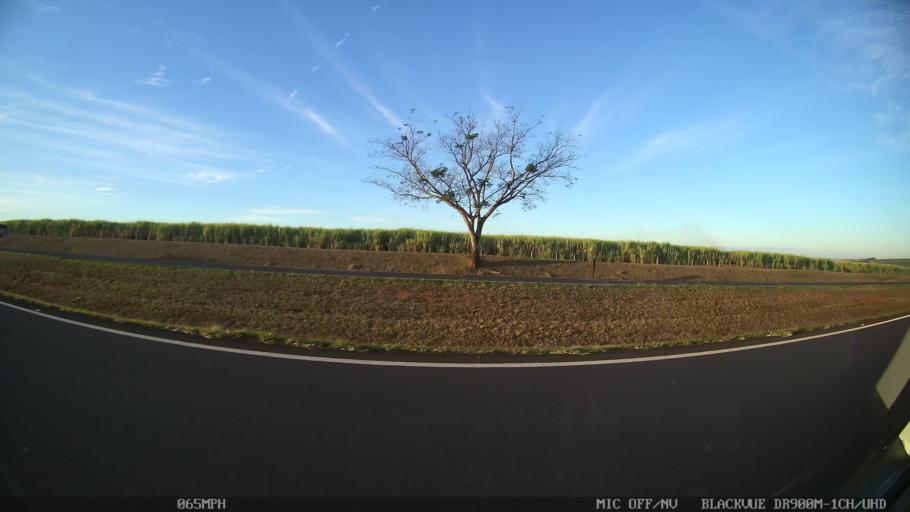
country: BR
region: Sao Paulo
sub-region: Catanduva
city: Catanduva
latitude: -21.1078
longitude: -49.0545
